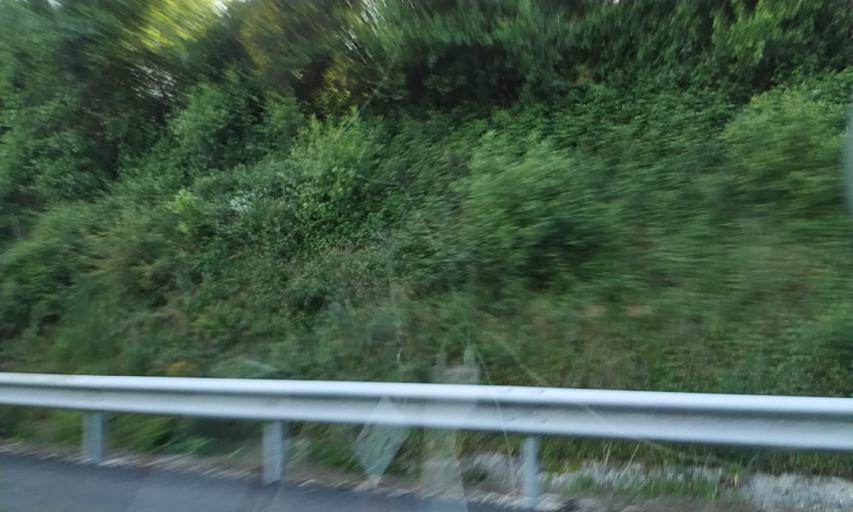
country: ES
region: Galicia
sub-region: Provincia de Pontevedra
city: Poio
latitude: 42.4746
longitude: -8.6601
